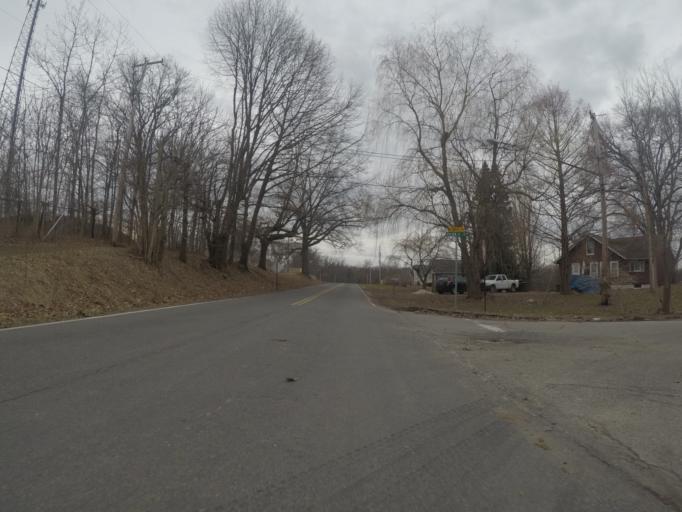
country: US
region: Ohio
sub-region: Portage County
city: Kent
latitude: 41.1704
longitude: -81.3110
